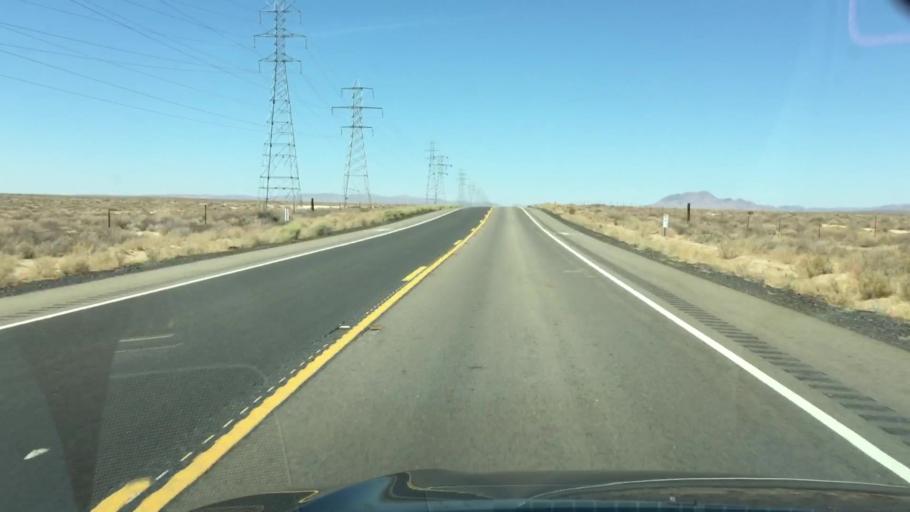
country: US
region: California
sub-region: Kern County
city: Boron
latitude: 35.1257
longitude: -117.5788
